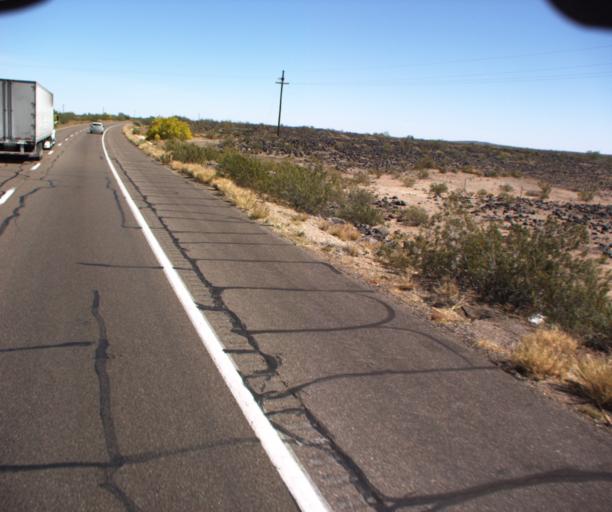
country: US
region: Arizona
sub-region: Maricopa County
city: Gila Bend
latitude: 32.8548
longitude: -113.2503
